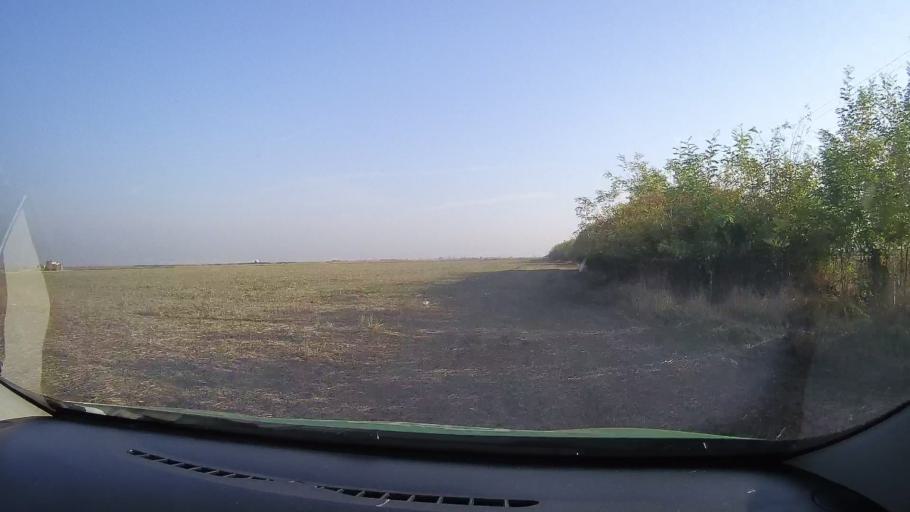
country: RO
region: Arad
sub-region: Comuna Graniceri
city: Graniceri
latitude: 46.5344
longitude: 21.3199
